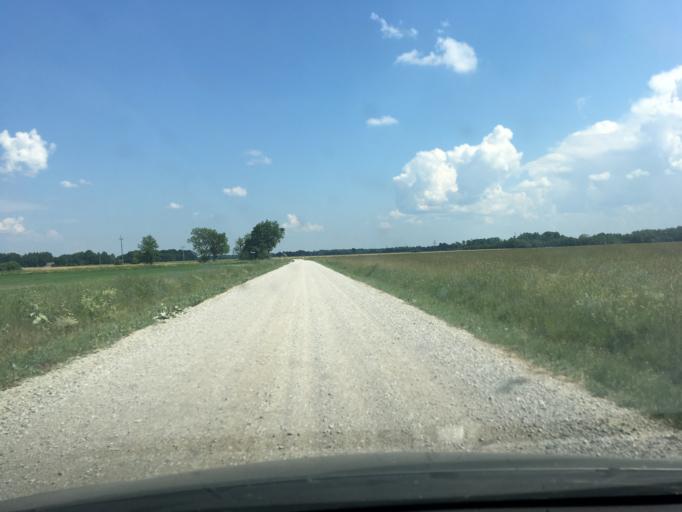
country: EE
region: Laeaene
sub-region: Lihula vald
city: Lihula
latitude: 58.7140
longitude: 24.0630
